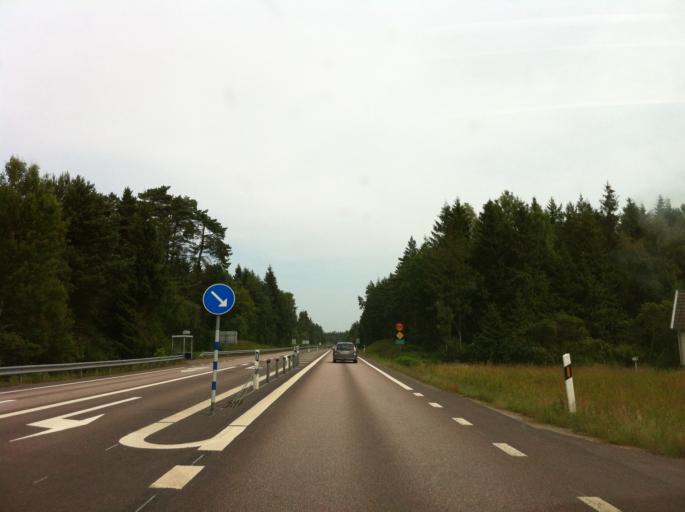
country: SE
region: Kalmar
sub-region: Torsas Kommun
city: Torsas
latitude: 56.2790
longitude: 15.9750
